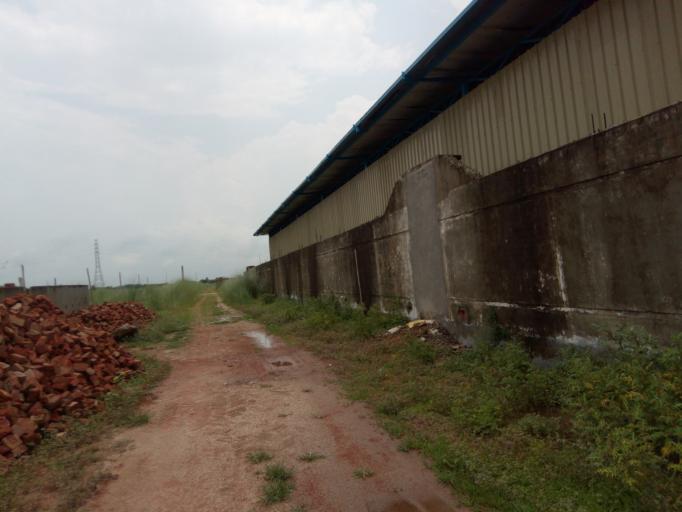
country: BD
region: Dhaka
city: Azimpur
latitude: 23.7514
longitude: 90.3383
